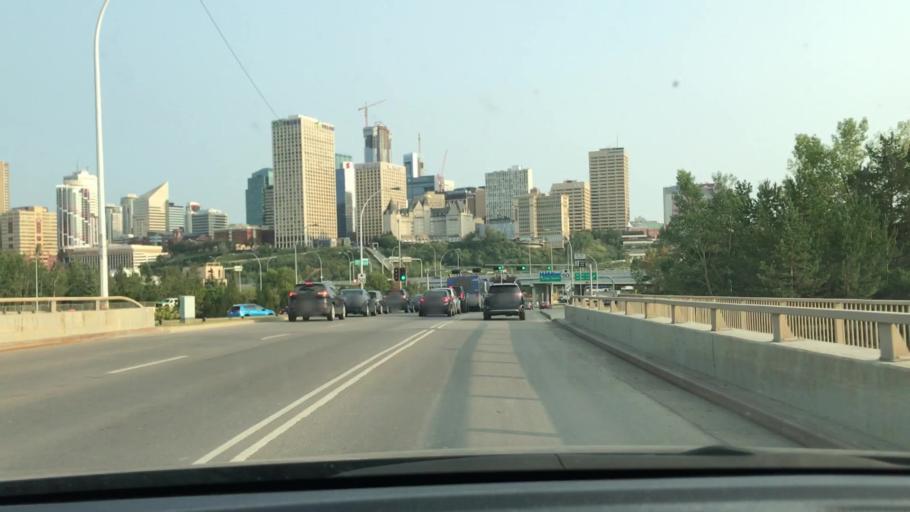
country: CA
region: Alberta
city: Edmonton
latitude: 53.5340
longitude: -113.4825
